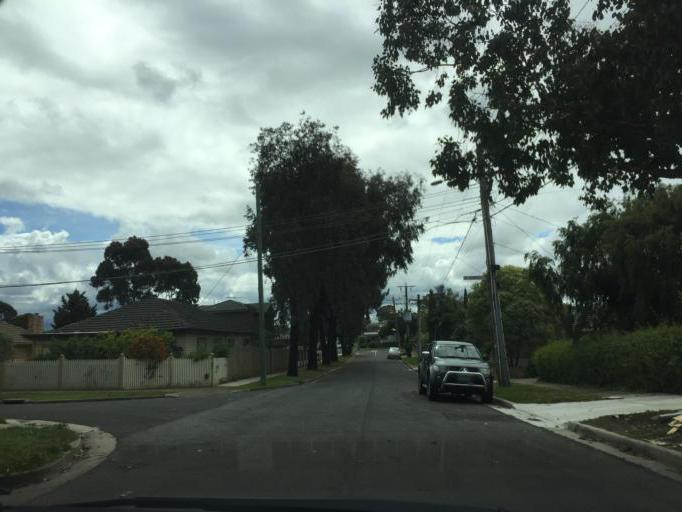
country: AU
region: Victoria
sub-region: Maribyrnong
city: Braybrook
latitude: -37.7929
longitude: 144.8424
